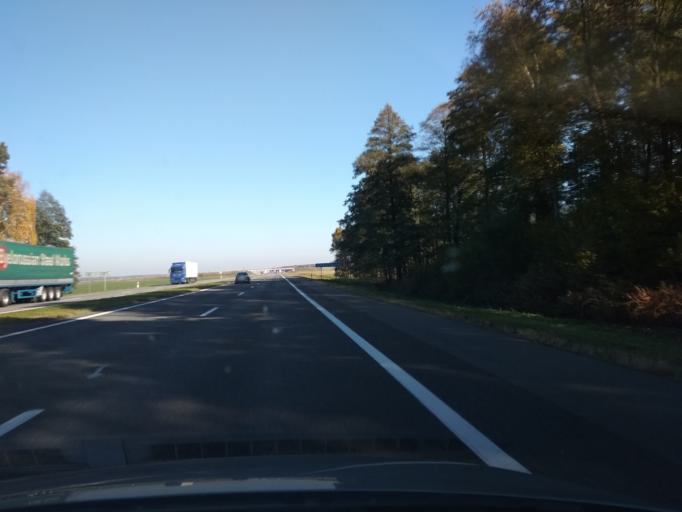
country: BY
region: Brest
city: Antopal'
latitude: 52.3828
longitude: 24.7638
